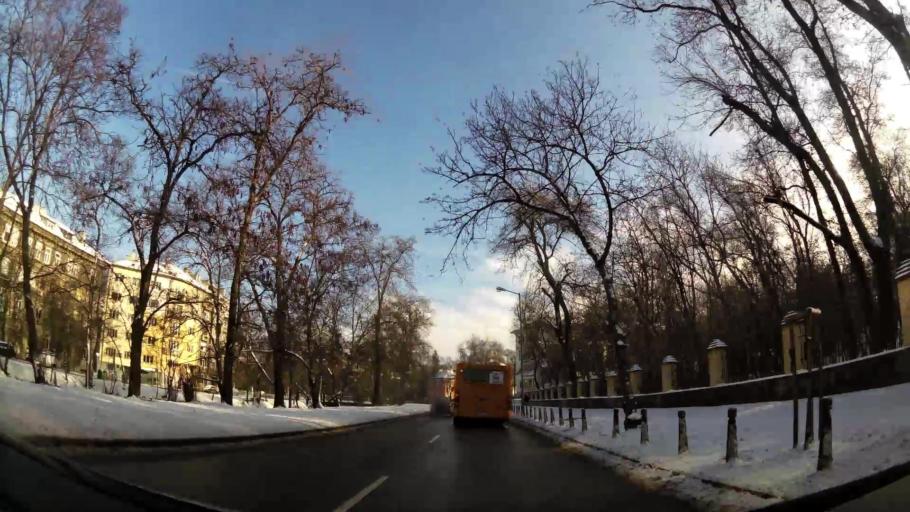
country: BG
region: Sofia-Capital
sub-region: Stolichna Obshtina
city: Sofia
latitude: 42.6929
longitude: 23.3455
